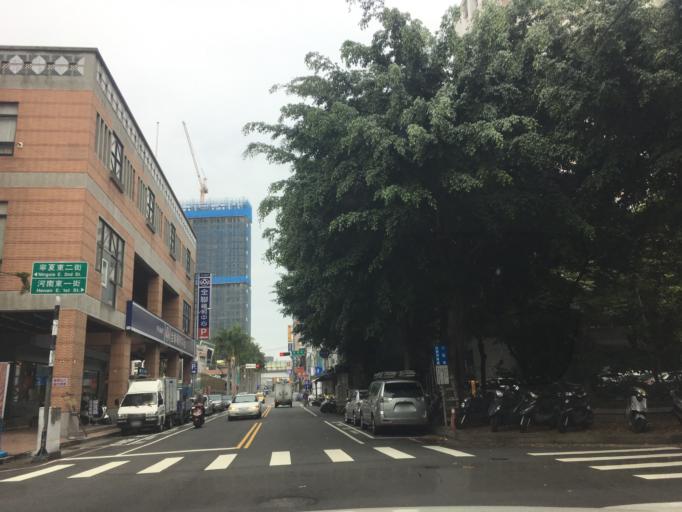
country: TW
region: Taiwan
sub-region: Taichung City
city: Taichung
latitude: 24.1692
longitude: 120.6624
